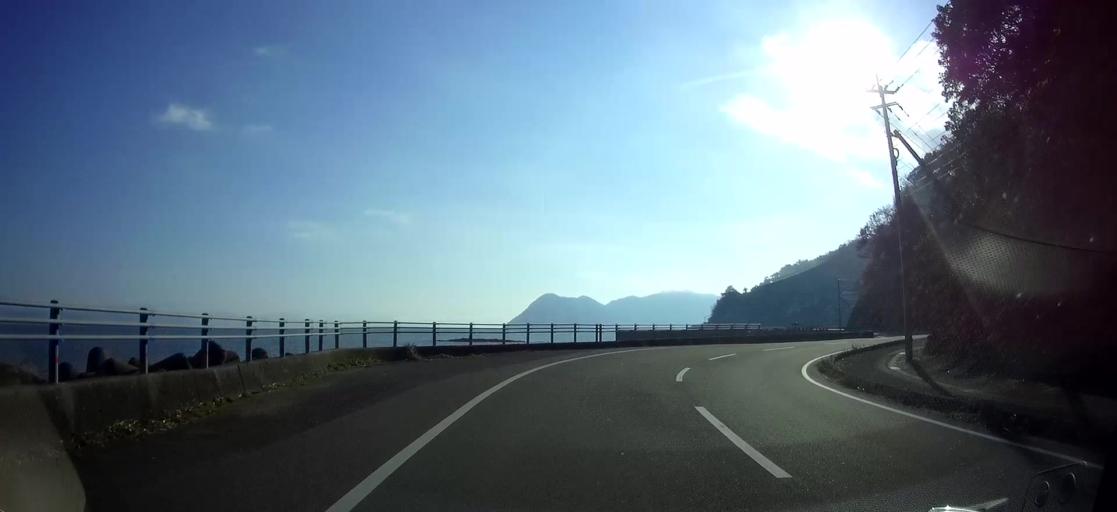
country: JP
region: Kumamoto
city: Minamata
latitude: 32.3889
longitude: 130.3855
